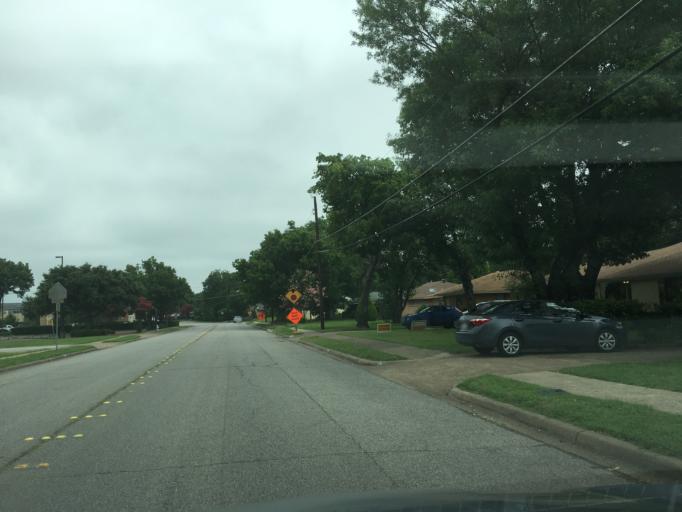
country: US
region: Texas
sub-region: Dallas County
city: Richardson
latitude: 32.9460
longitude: -96.7281
